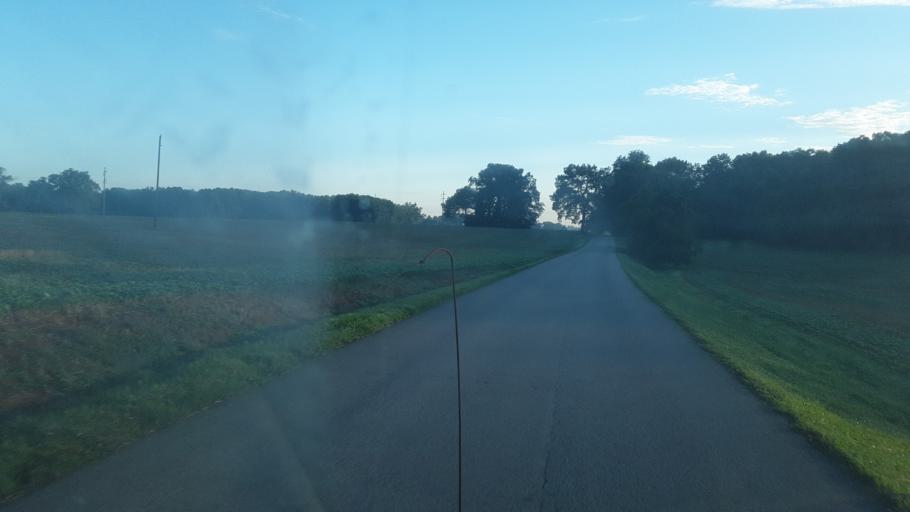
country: US
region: Kentucky
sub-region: Todd County
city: Guthrie
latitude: 36.7133
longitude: -87.1715
